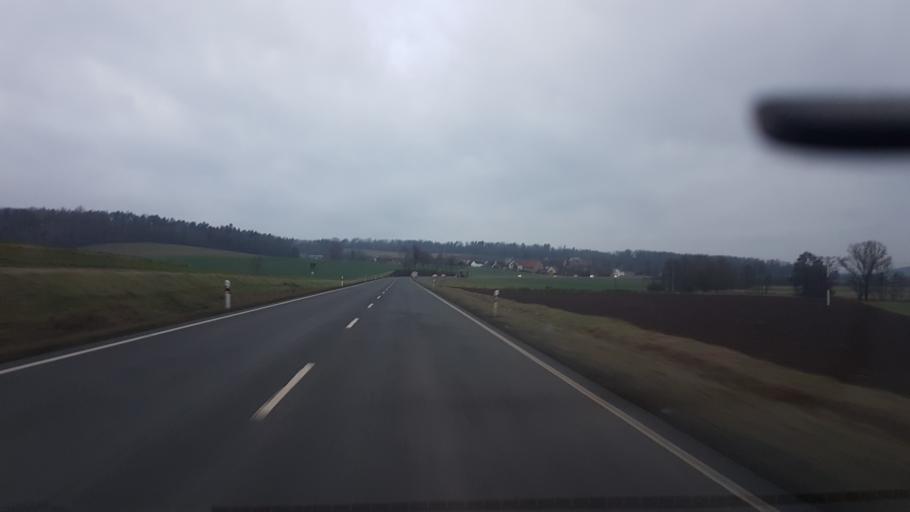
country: DE
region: Bavaria
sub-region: Upper Franconia
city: Gerach
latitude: 50.0411
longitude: 10.8178
